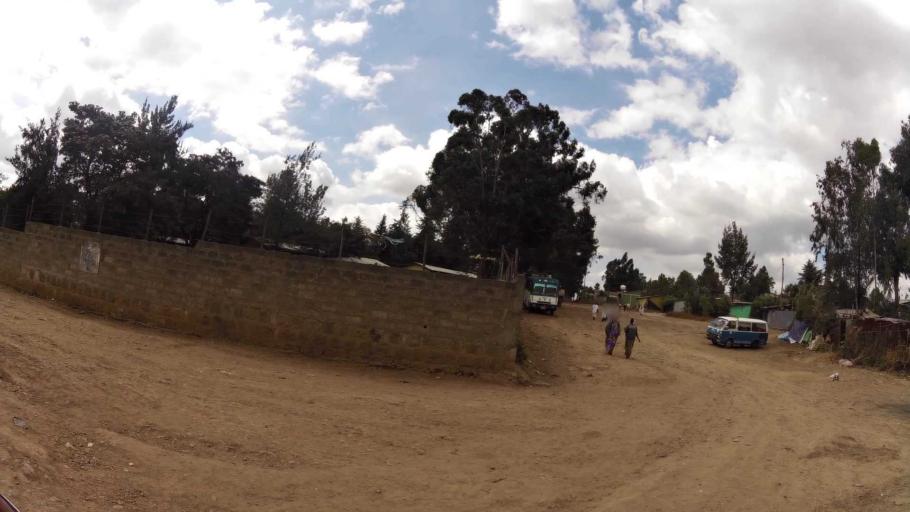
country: ET
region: Adis Abeba
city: Addis Ababa
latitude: 8.9467
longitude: 38.7541
